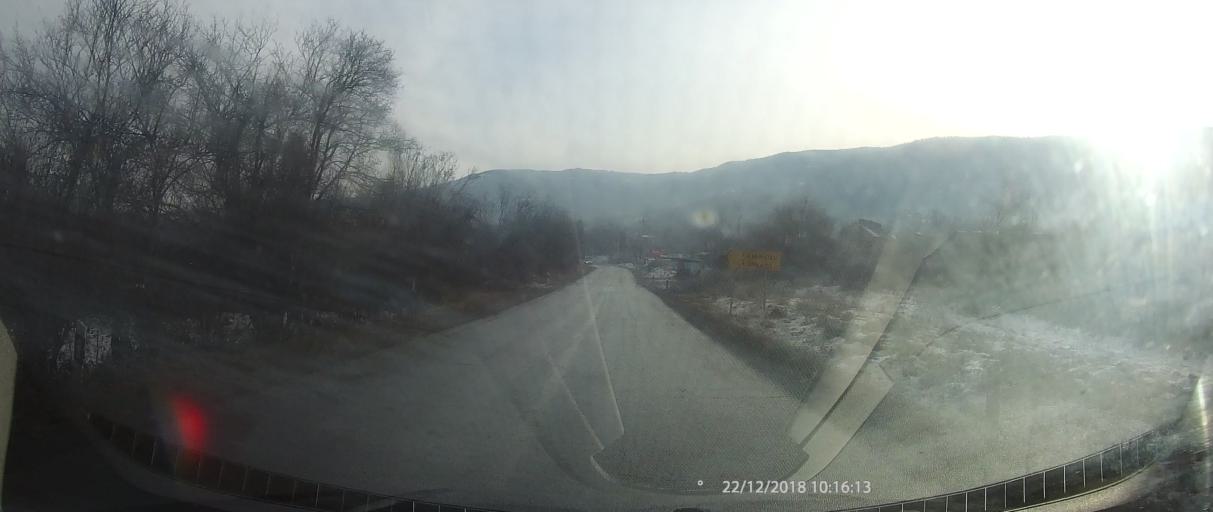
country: MK
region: Kriva Palanka
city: Kriva Palanka
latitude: 42.1789
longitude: 22.2631
